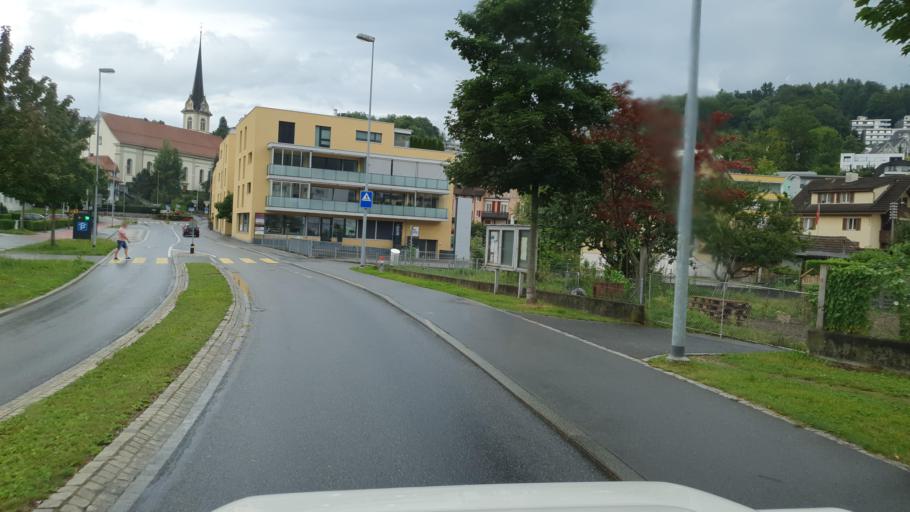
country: CH
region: Lucerne
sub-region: Lucerne-Land District
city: Horw
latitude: 47.0182
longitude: 8.3096
